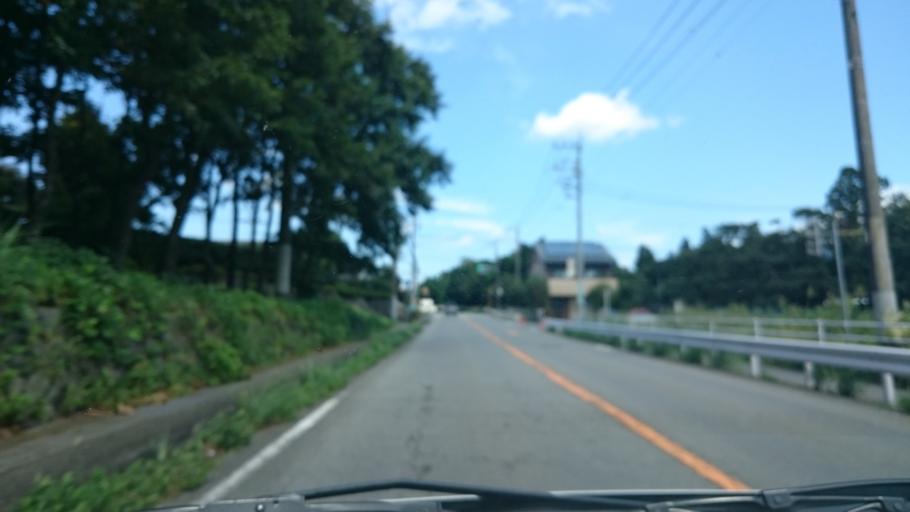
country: JP
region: Shizuoka
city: Gotemba
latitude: 35.2368
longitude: 138.9208
